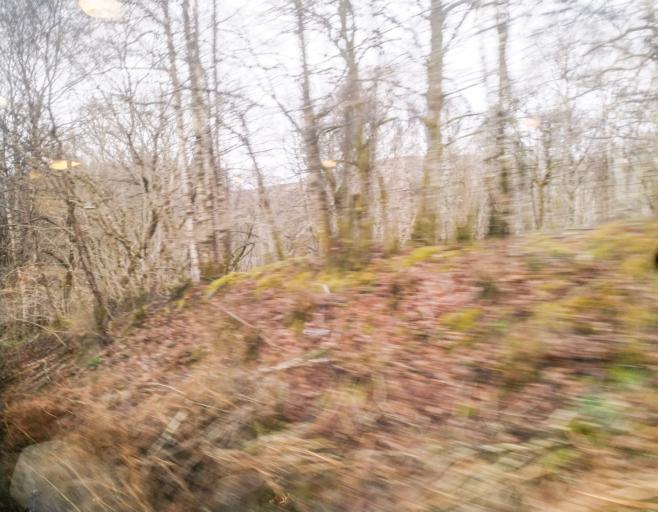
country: GB
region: Scotland
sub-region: Highland
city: Spean Bridge
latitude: 56.8902
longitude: -4.8760
